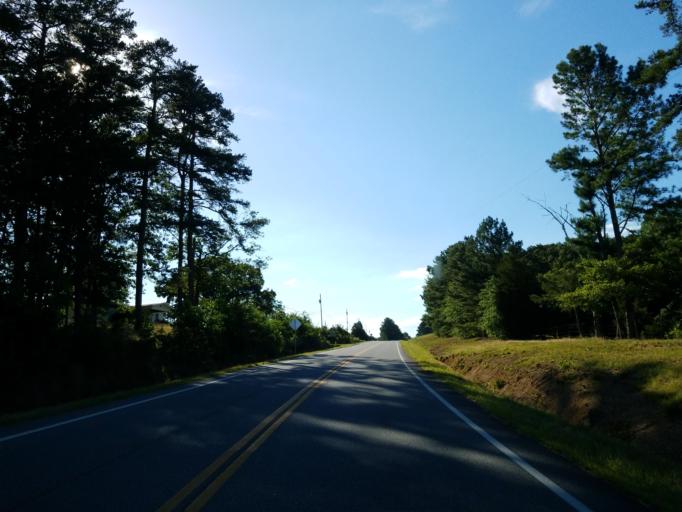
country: US
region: Georgia
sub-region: Gordon County
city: Calhoun
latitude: 34.5887
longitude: -85.0181
